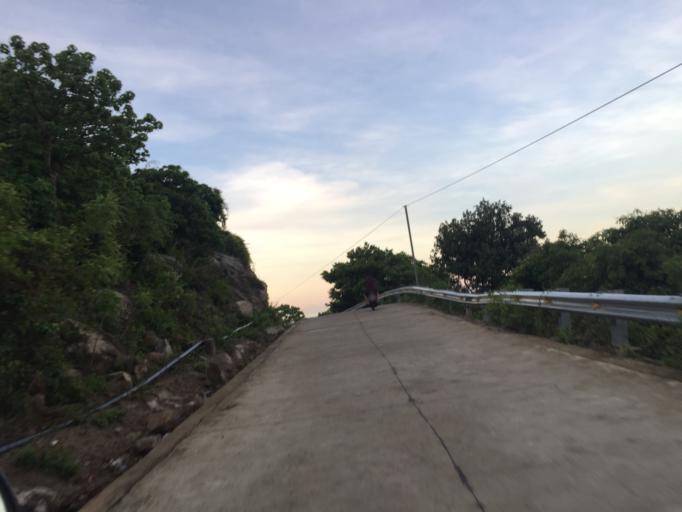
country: VN
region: Quang Nam
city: Hoi An
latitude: 15.9532
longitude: 108.5086
